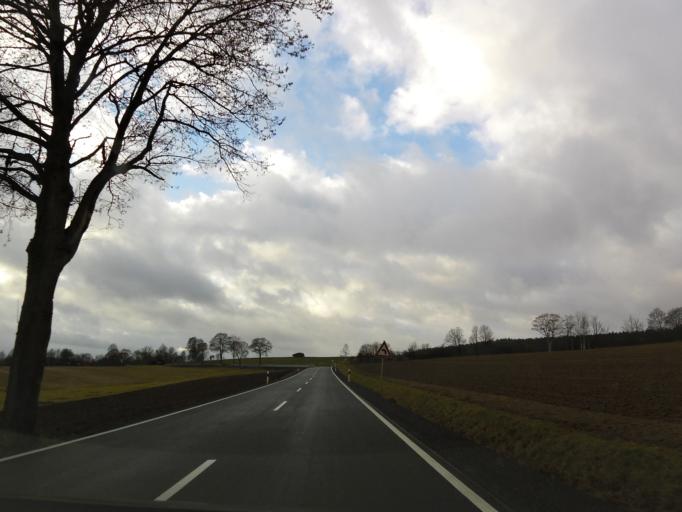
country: DE
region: Bavaria
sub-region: Upper Franconia
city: Hochstadt bei Thiersheim
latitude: 50.0762
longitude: 12.0655
